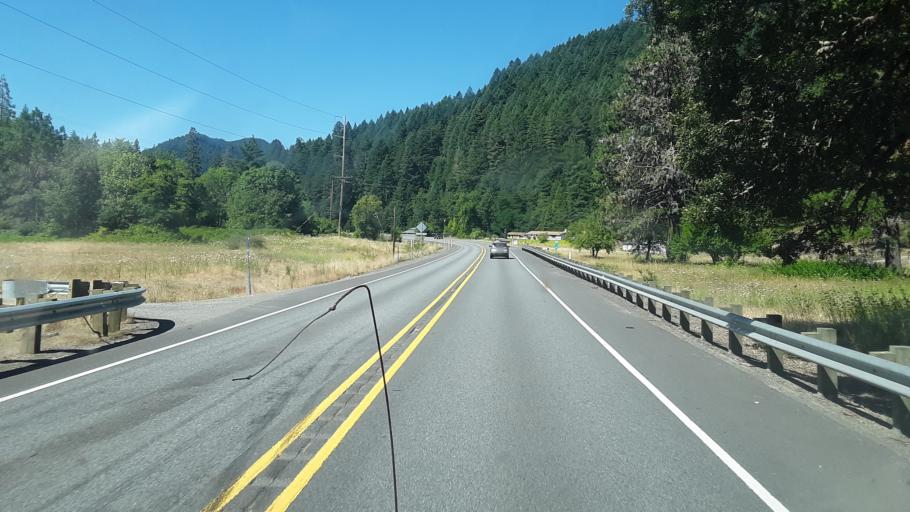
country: US
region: Oregon
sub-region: Josephine County
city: Redwood
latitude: 42.3774
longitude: -123.4959
